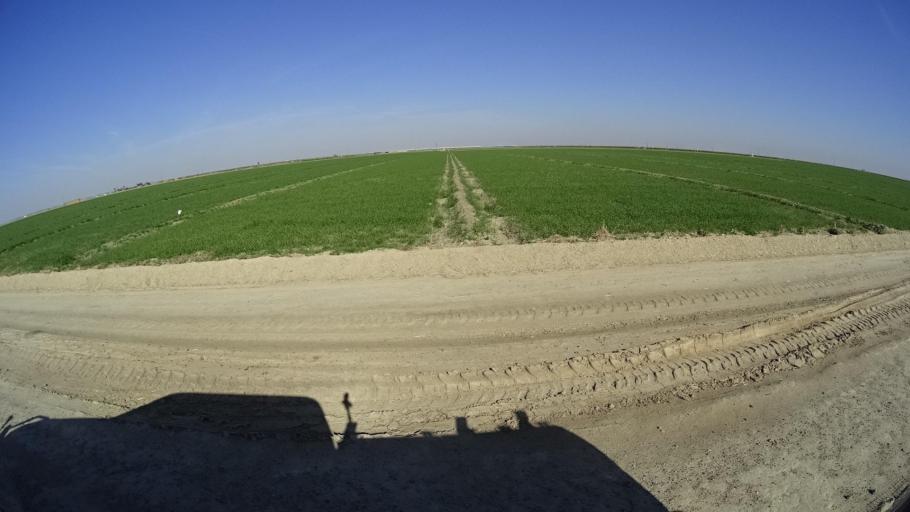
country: US
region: California
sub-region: Kern County
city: Wasco
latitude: 35.7175
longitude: -119.4146
